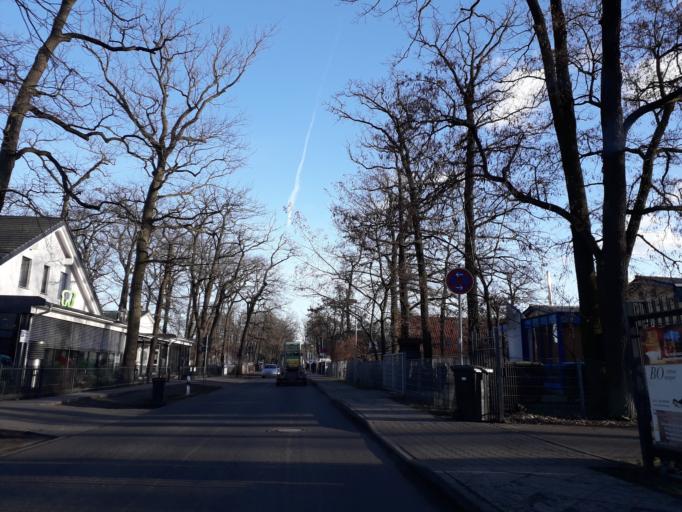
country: DE
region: Brandenburg
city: Brieselang
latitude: 52.5805
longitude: 12.9997
